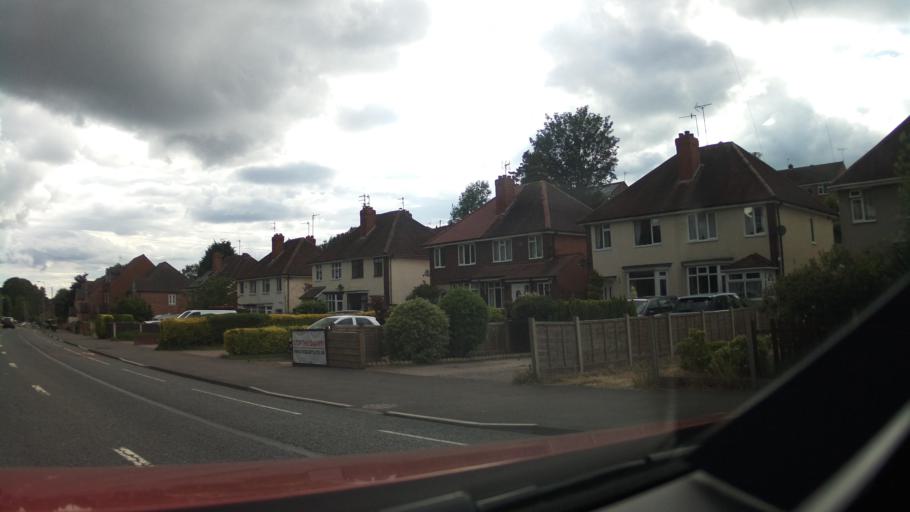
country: GB
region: England
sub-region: Worcestershire
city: Kidderminster
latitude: 52.4026
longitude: -2.2298
